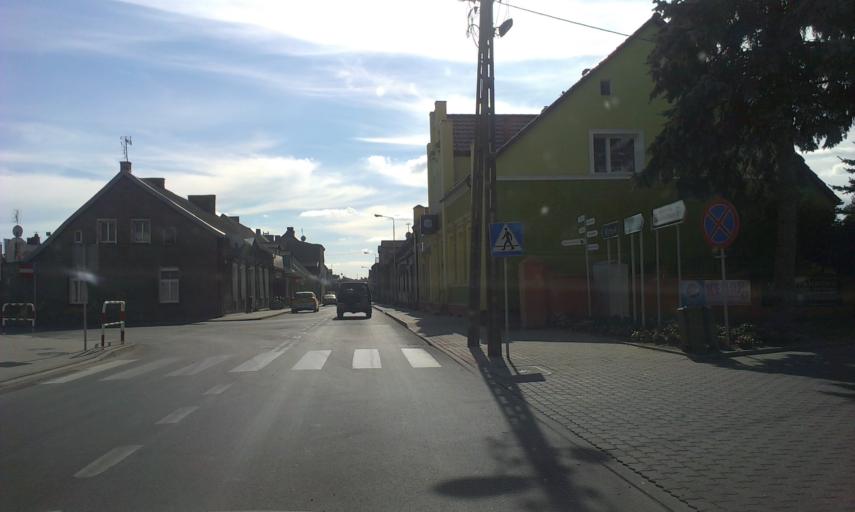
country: PL
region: Greater Poland Voivodeship
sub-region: Powiat pilski
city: Lobzenica
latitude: 53.2622
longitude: 17.2557
